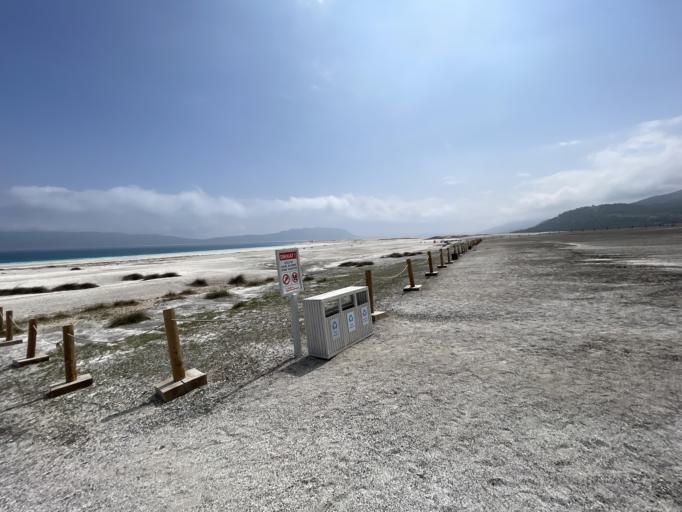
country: TR
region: Burdur
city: Yesilova
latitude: 37.5349
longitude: 29.6453
